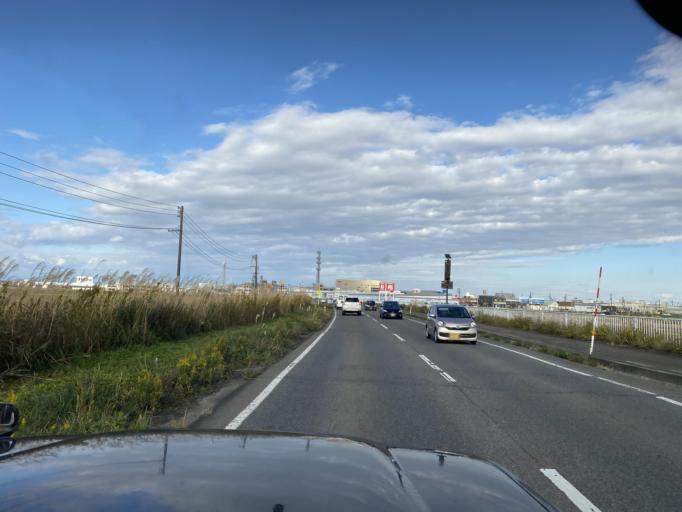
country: JP
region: Niigata
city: Niitsu-honcho
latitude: 37.7820
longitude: 139.1109
